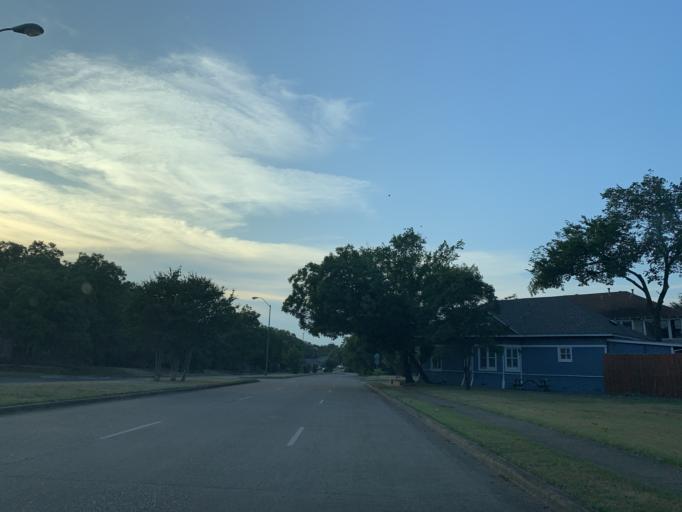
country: US
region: Texas
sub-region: Dallas County
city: Cockrell Hill
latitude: 32.7422
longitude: -96.8412
